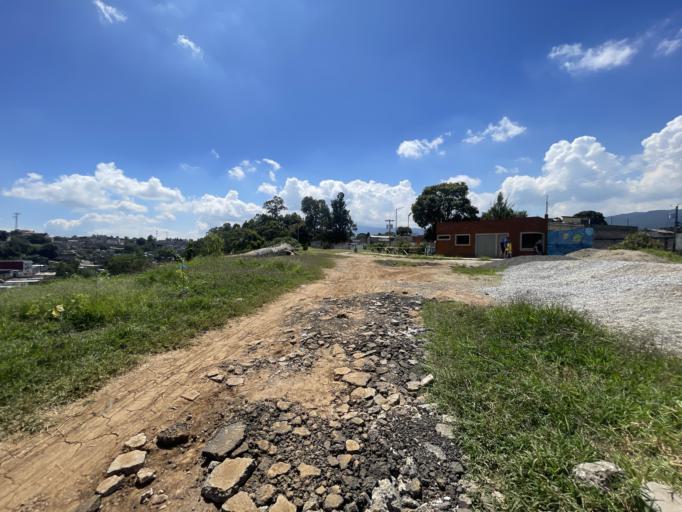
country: GT
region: Guatemala
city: Mixco
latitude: 14.6637
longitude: -90.5814
